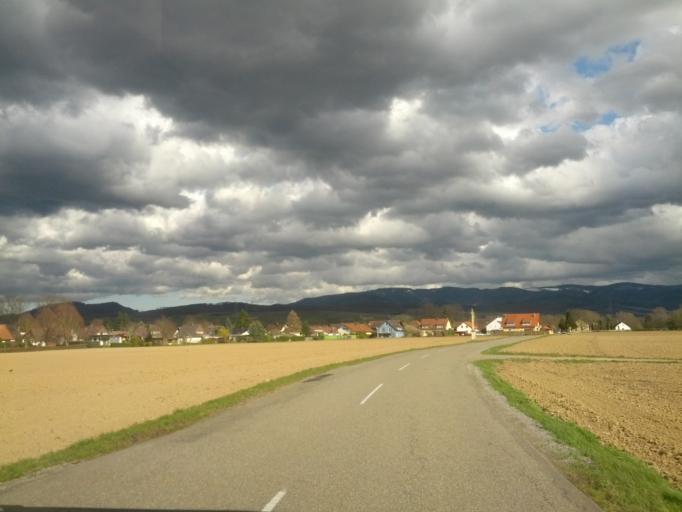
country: DE
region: Baden-Wuerttemberg
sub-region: Freiburg Region
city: Bad Krozingen
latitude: 47.9348
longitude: 7.7045
